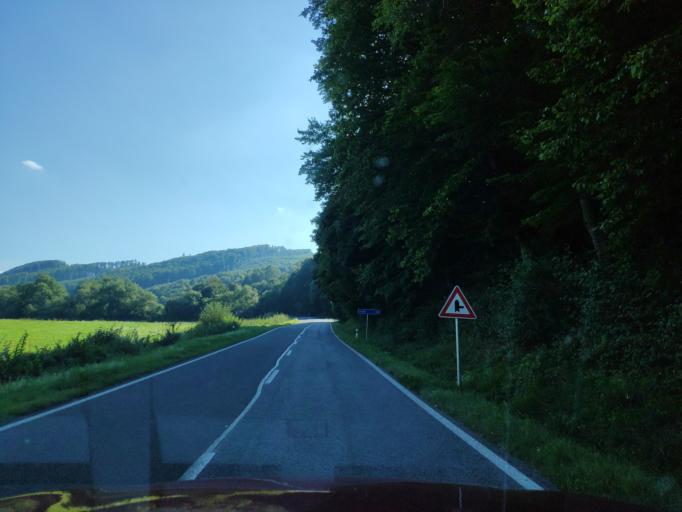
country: SK
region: Presovsky
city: Snina
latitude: 49.0367
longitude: 22.2511
